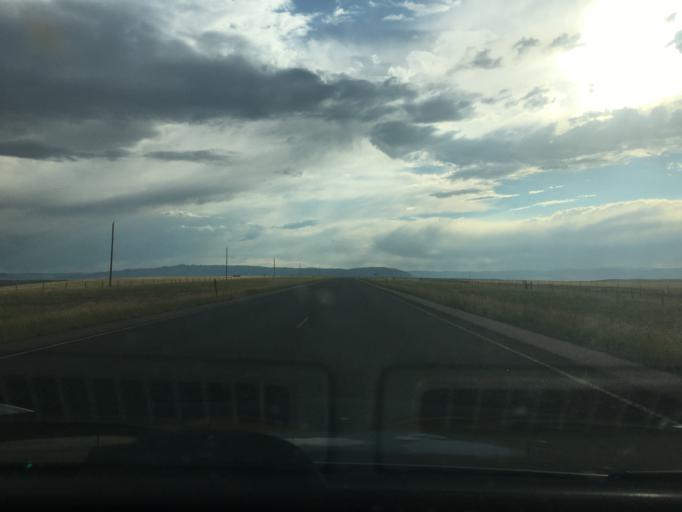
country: US
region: Wyoming
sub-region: Albany County
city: Laramie
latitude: 41.3223
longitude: -105.7488
